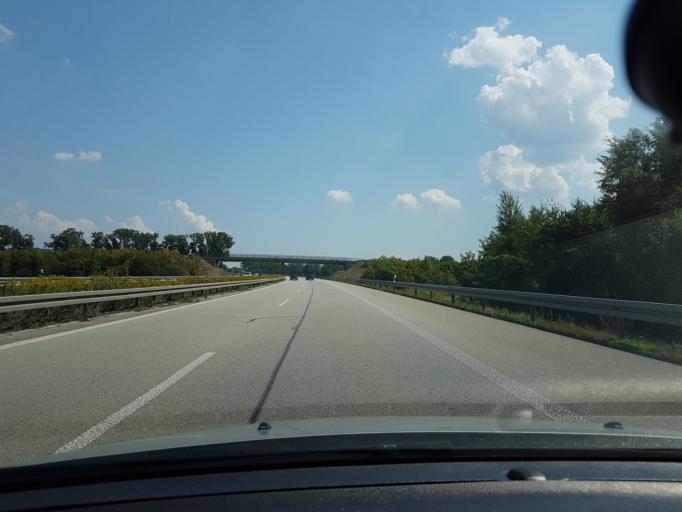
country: DE
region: Bavaria
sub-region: Upper Bavaria
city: Winhoring
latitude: 48.2525
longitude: 12.6379
